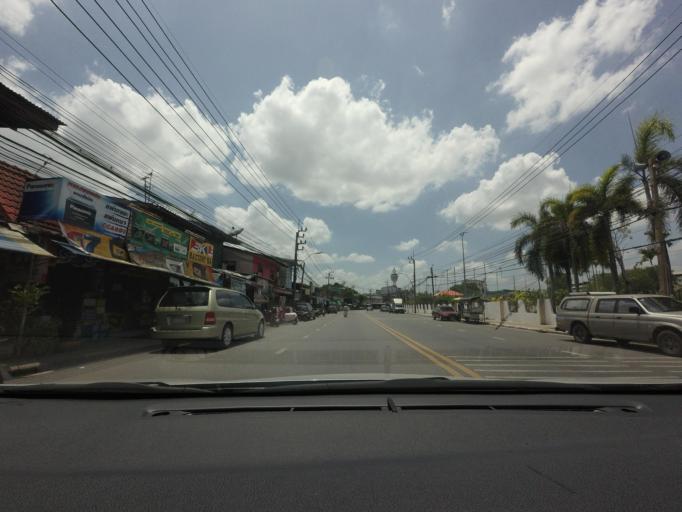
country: TH
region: Samut Prakan
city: Samut Prakan
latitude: 13.5882
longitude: 100.5960
